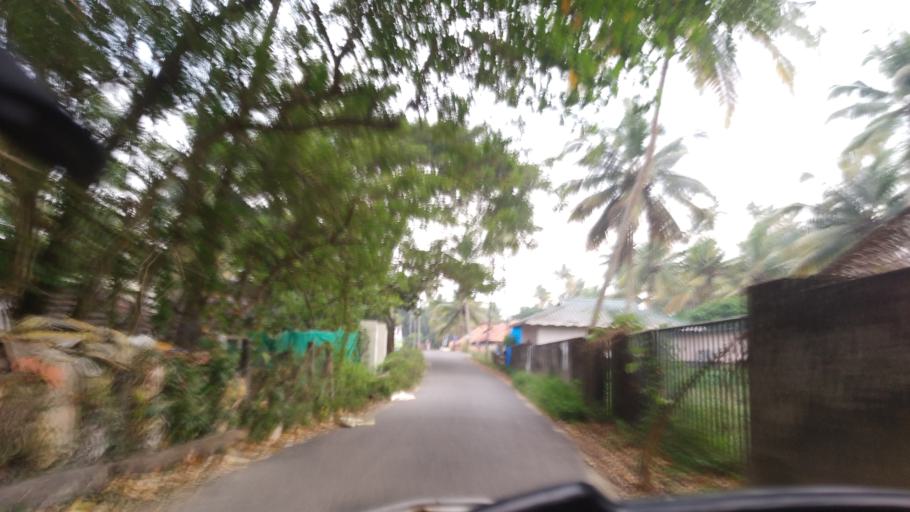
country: IN
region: Kerala
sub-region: Thrissur District
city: Kodungallur
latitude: 10.1392
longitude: 76.1998
